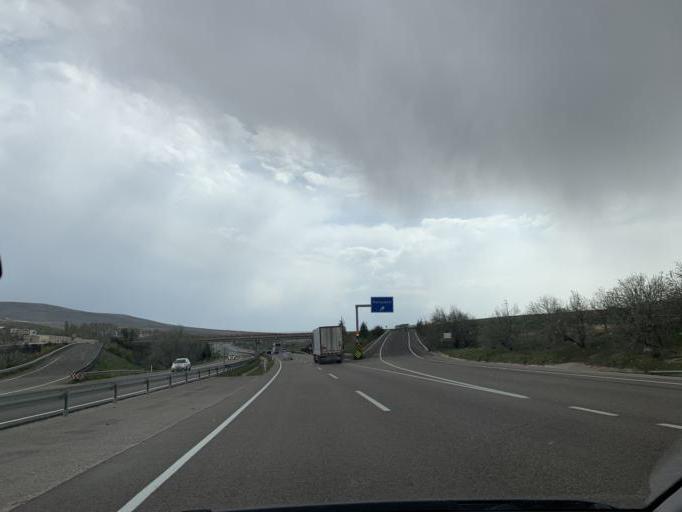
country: TR
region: Eskisehir
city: Sivrihisar
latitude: 39.4947
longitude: 31.6019
